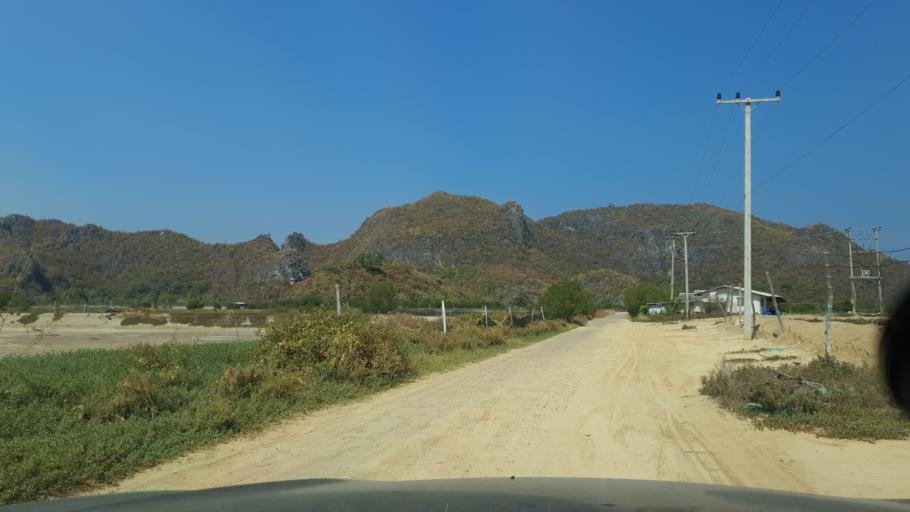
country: TH
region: Prachuap Khiri Khan
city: Sam Roi Yot
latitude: 12.1954
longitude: 99.9910
